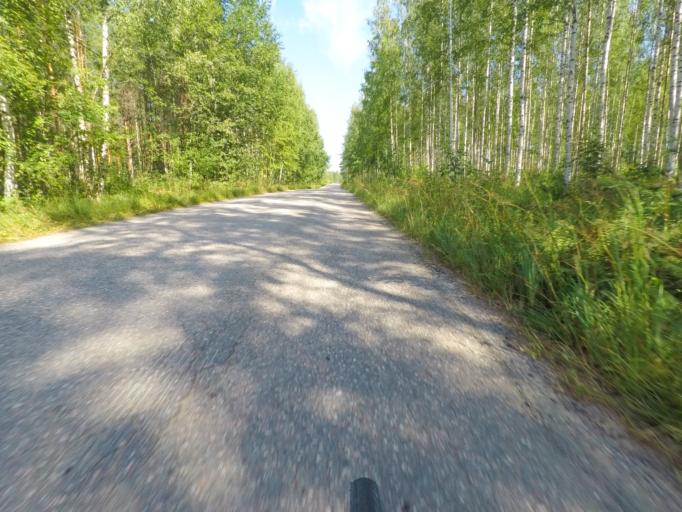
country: FI
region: Southern Savonia
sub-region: Mikkeli
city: Puumala
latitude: 61.4215
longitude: 28.1215
